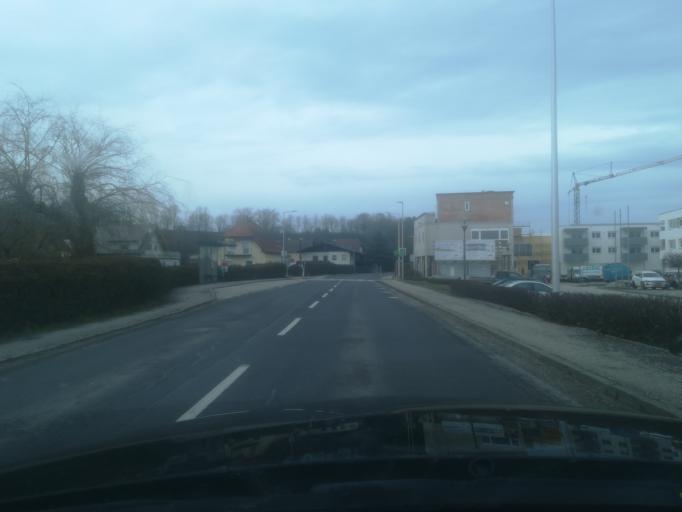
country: AT
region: Upper Austria
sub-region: Wels-Land
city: Lambach
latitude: 48.0946
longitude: 13.8951
